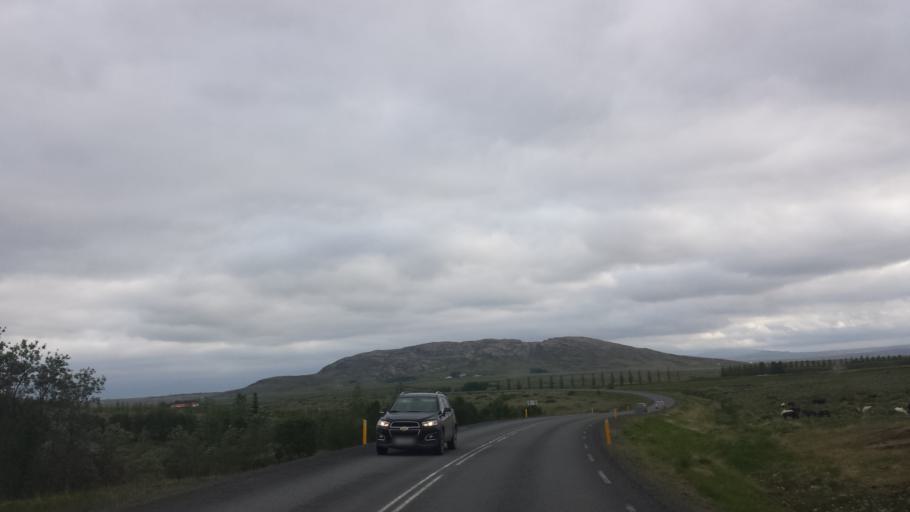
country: IS
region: South
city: Selfoss
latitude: 64.1562
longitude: -20.5404
